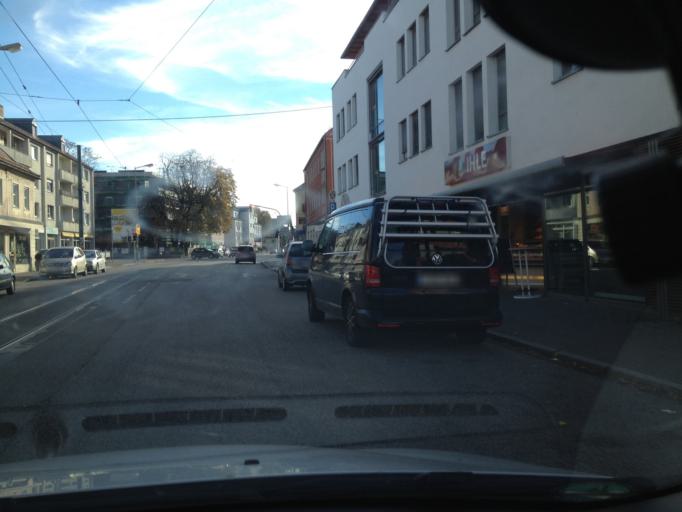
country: DE
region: Bavaria
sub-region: Swabia
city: Stadtbergen
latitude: 48.3391
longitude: 10.8681
